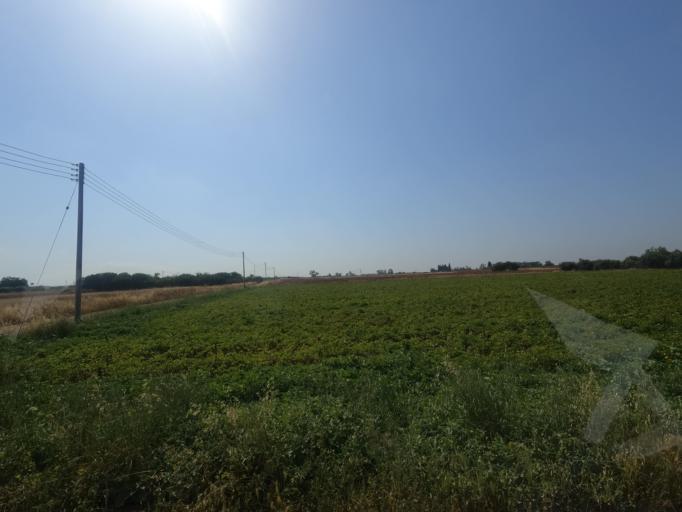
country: CY
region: Ammochostos
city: Avgorou
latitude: 35.0519
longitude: 33.8529
